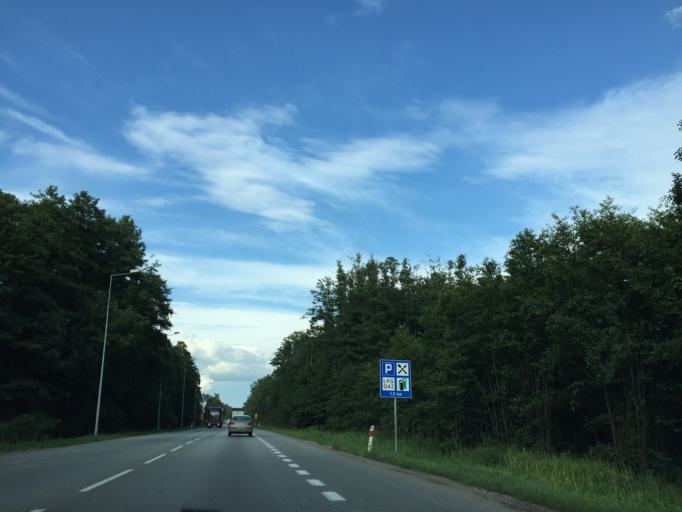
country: PL
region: Masovian Voivodeship
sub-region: Powiat otwocki
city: Karczew
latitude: 52.0129
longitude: 21.2814
